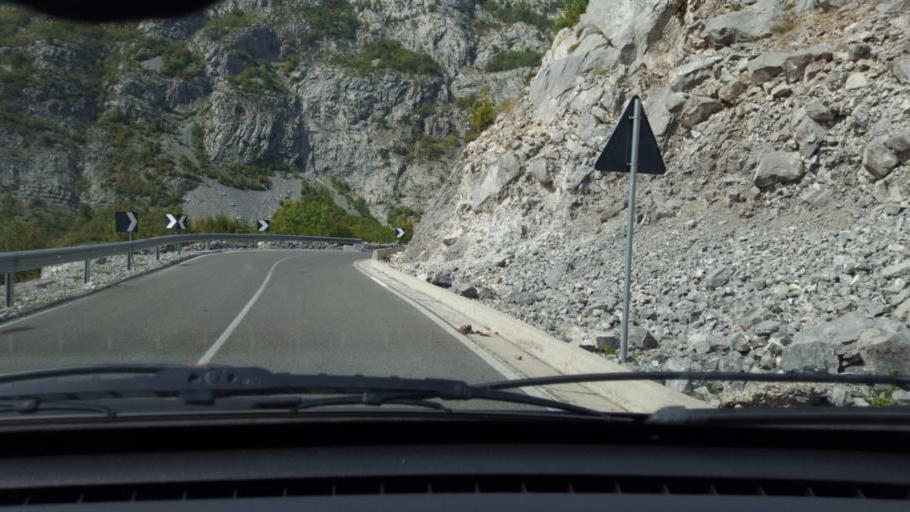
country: AL
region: Shkoder
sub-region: Rrethi i Malesia e Madhe
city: Kastrat
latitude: 42.5114
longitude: 19.6182
